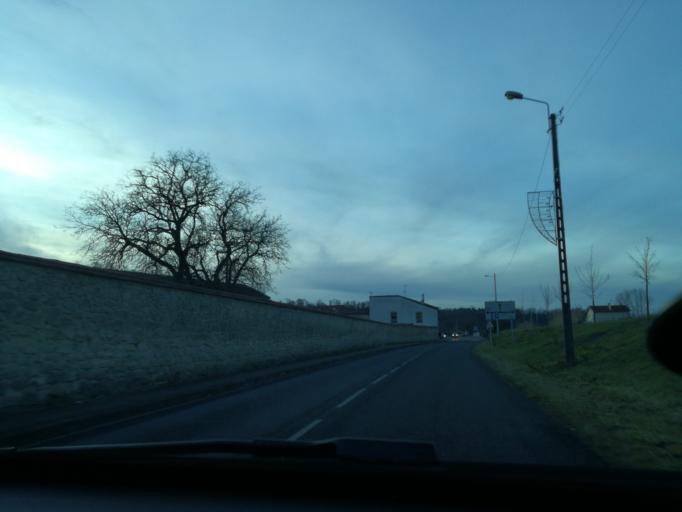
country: FR
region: Lorraine
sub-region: Departement de la Meuse
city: Fains-Veel
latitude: 48.7921
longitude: 5.1286
